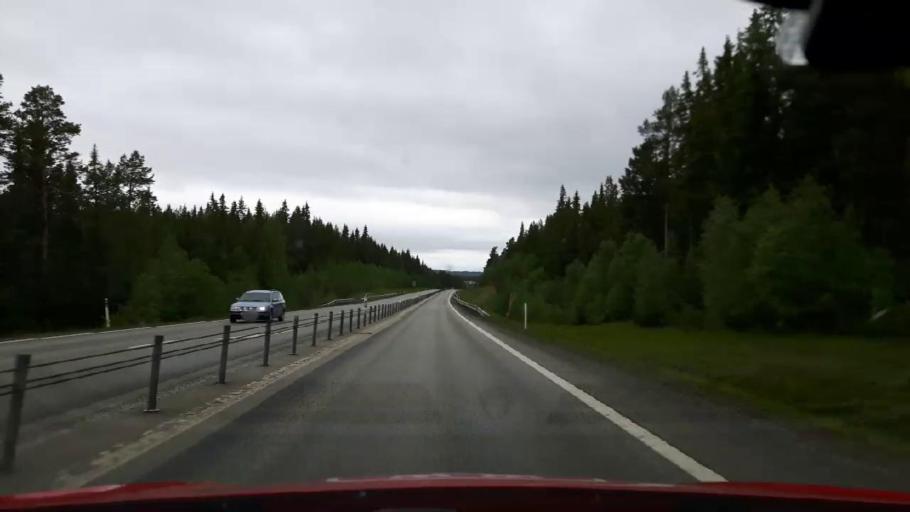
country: SE
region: Jaemtland
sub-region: OEstersunds Kommun
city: Ostersund
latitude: 63.1673
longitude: 14.7187
